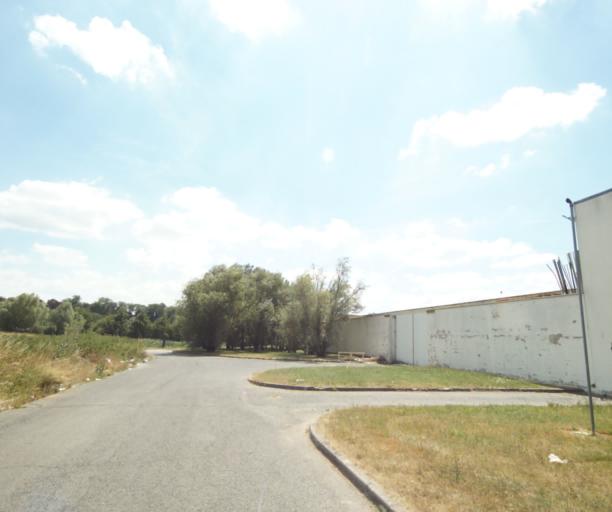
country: FR
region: Lorraine
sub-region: Departement de Meurthe-et-Moselle
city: Luneville
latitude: 48.5994
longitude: 6.4966
